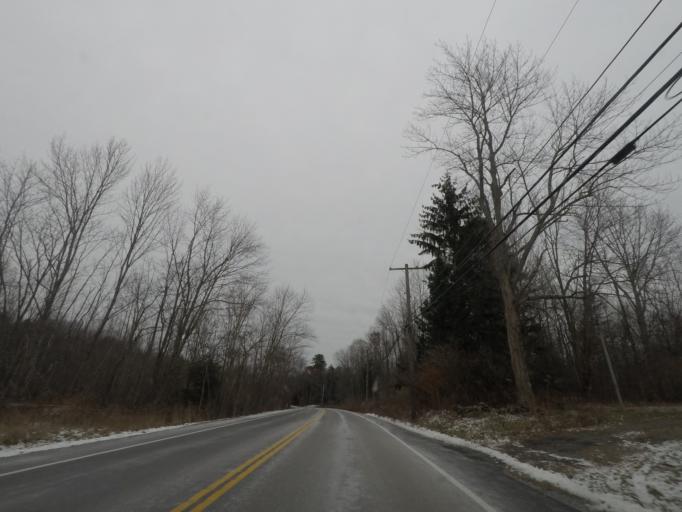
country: US
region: New York
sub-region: Rensselaer County
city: Hoosick Falls
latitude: 42.7611
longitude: -73.3871
